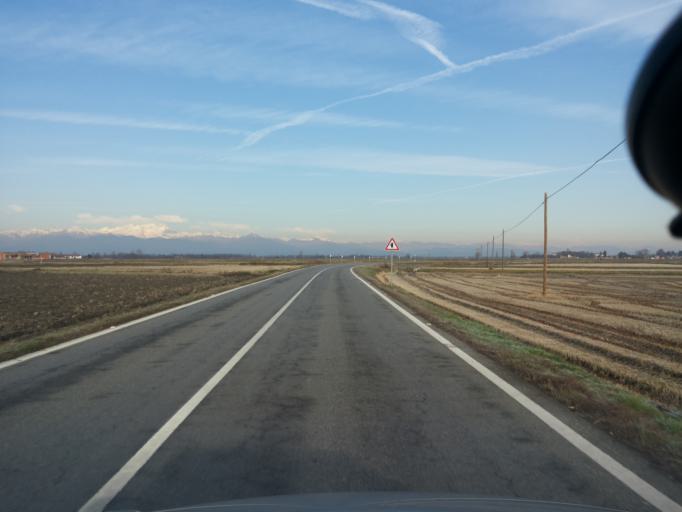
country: IT
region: Piedmont
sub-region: Provincia di Vercelli
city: Oldenico
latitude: 45.4066
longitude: 8.3776
